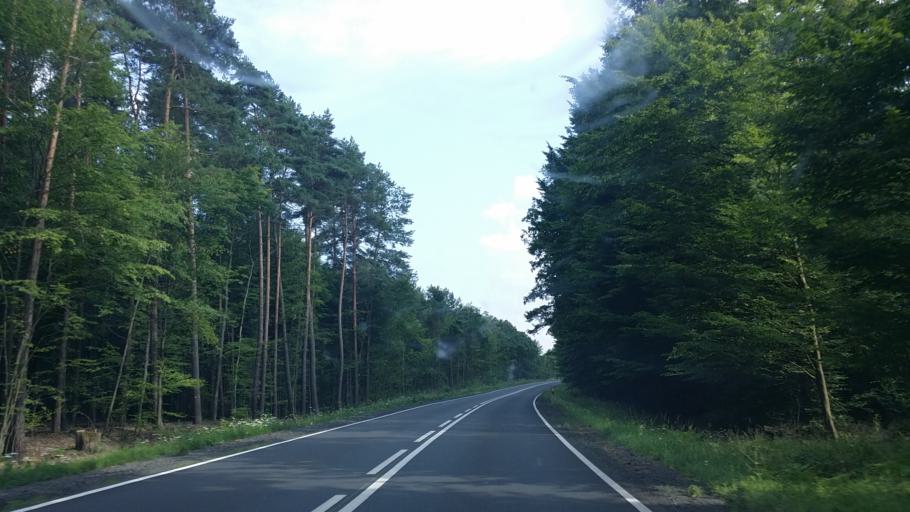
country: PL
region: Lubusz
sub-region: Powiat gorzowski
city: Klodawa
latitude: 52.8739
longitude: 15.2022
